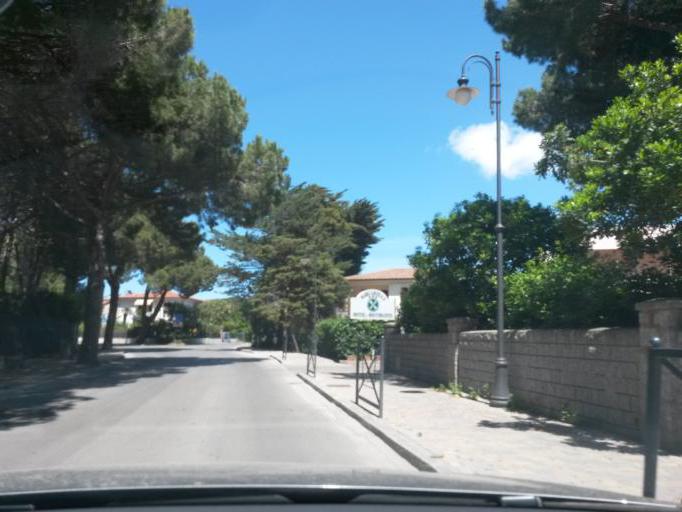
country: IT
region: Tuscany
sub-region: Provincia di Livorno
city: Campo nell'Elba
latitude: 42.7480
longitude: 10.2348
